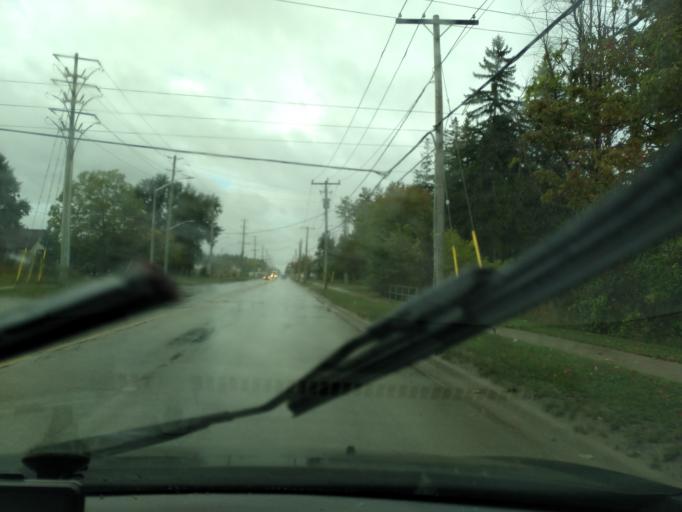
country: CA
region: Ontario
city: Barrie
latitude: 44.3703
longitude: -79.7099
